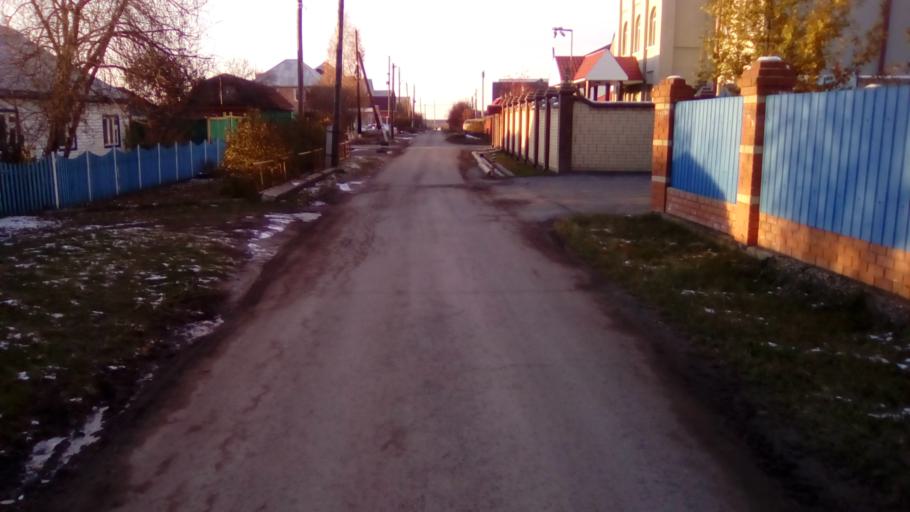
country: RU
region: Tjumen
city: Moskovskiy
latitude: 57.2210
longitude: 65.3649
